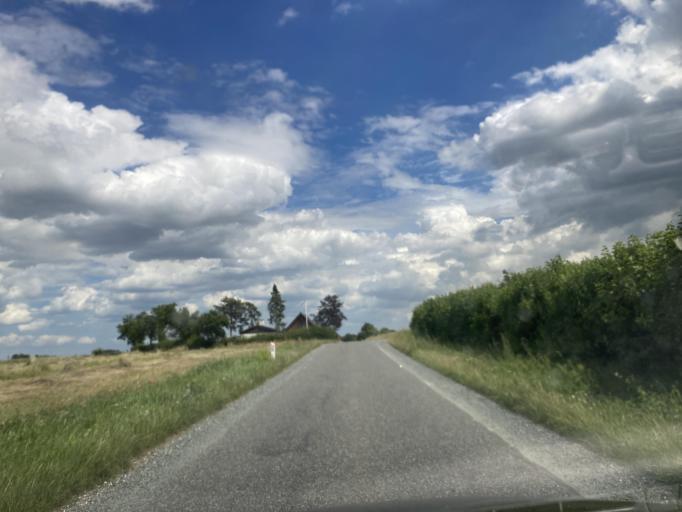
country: DK
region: Zealand
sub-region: Faxe Kommune
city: Haslev
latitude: 55.3573
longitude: 11.9603
